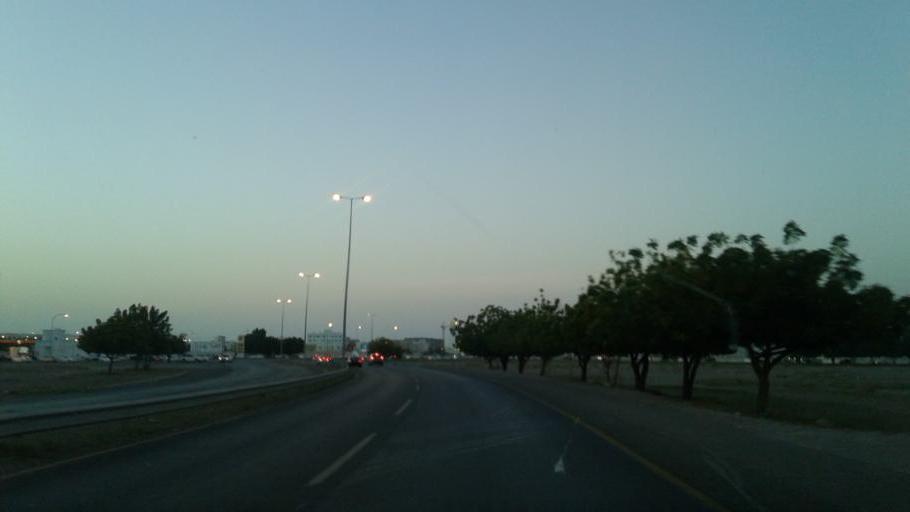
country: OM
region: Muhafazat Masqat
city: As Sib al Jadidah
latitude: 23.6116
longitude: 58.2156
